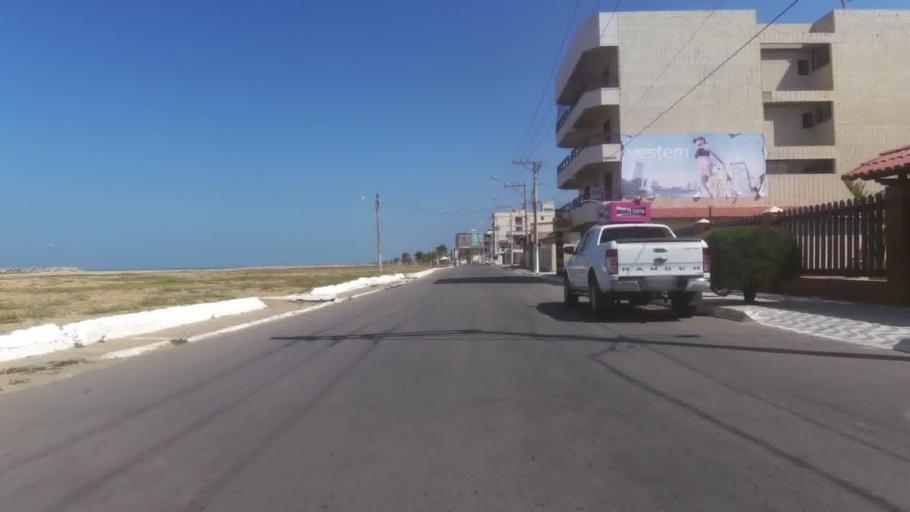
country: BR
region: Espirito Santo
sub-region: Marataizes
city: Marataizes
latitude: -21.0471
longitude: -40.8297
